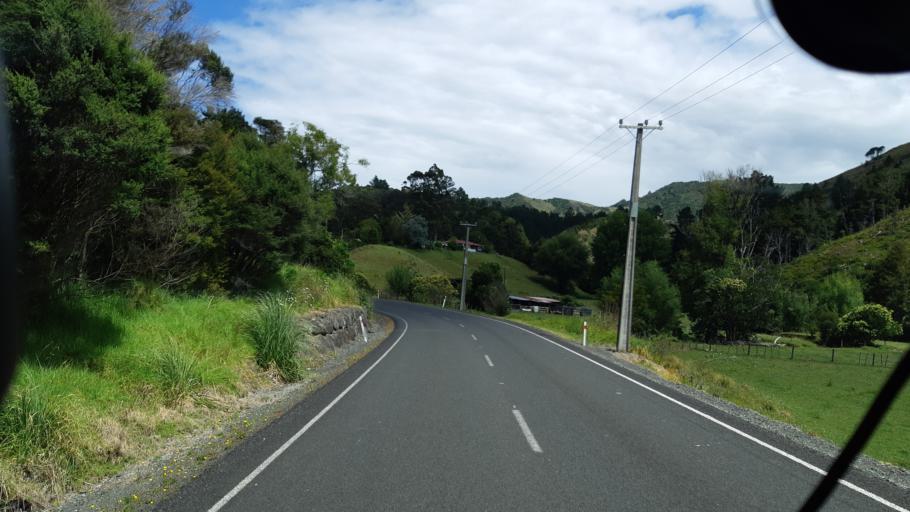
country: NZ
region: Northland
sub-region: Far North District
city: Taipa
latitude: -35.2668
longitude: 173.5020
